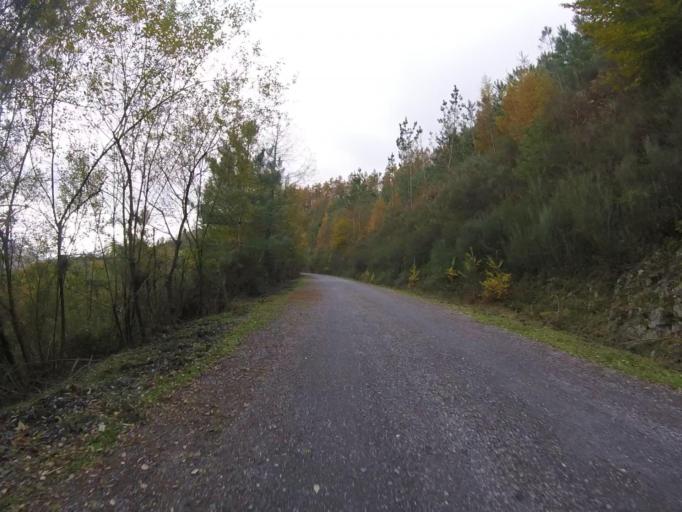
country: ES
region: Navarre
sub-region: Provincia de Navarra
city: Goizueta
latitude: 43.2233
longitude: -1.8238
